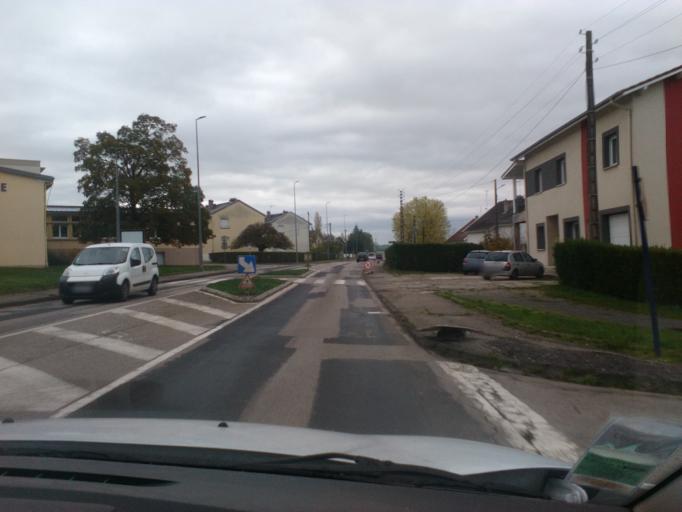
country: FR
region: Lorraine
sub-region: Departement des Vosges
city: Rambervillers
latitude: 48.3328
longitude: 6.6367
